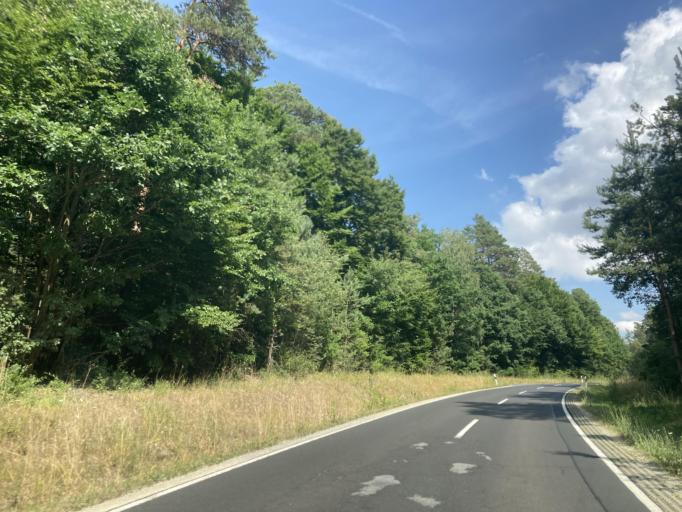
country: DE
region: Hesse
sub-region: Regierungsbezirk Kassel
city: Grossenluder
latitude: 50.5432
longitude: 9.5396
